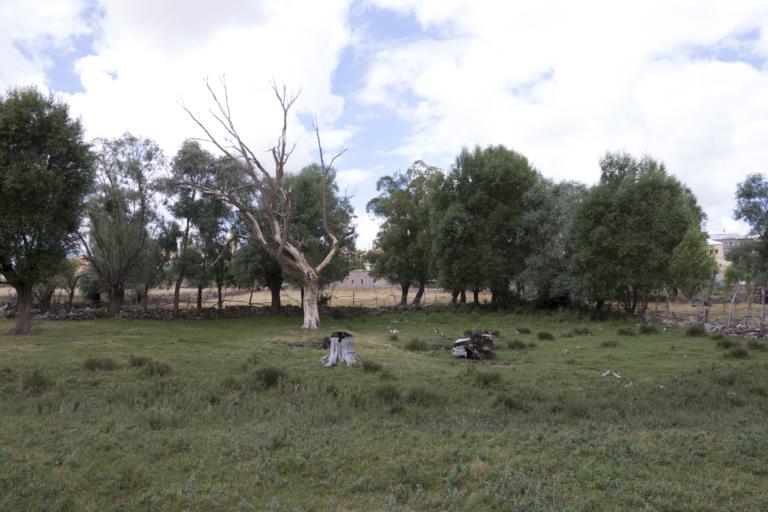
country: TR
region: Kayseri
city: Toklar
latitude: 38.4215
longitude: 36.0970
